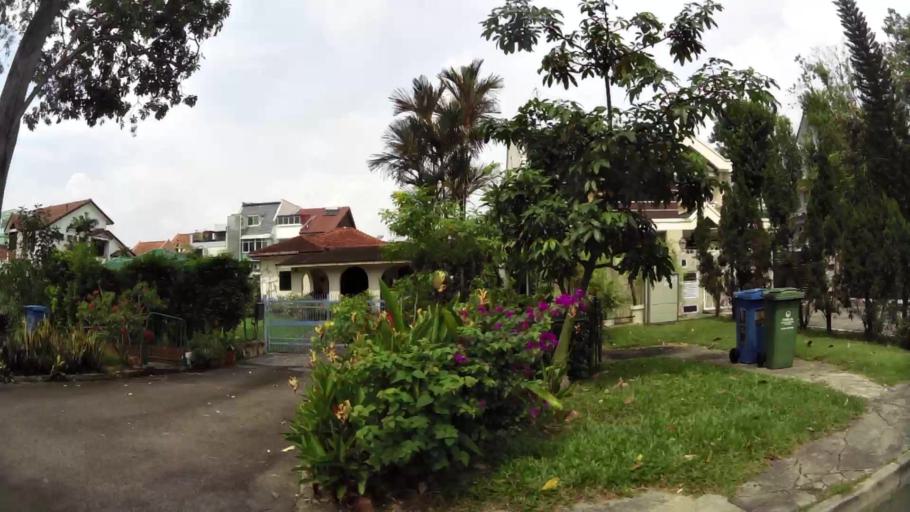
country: MY
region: Johor
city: Kampung Pasir Gudang Baru
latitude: 1.3646
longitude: 103.9750
